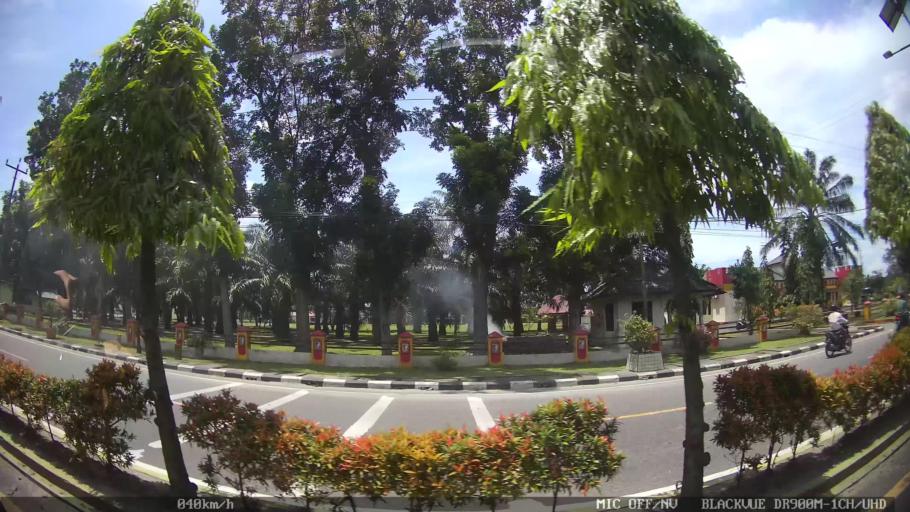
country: ID
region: North Sumatra
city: Binjai
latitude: 3.6086
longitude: 98.5056
